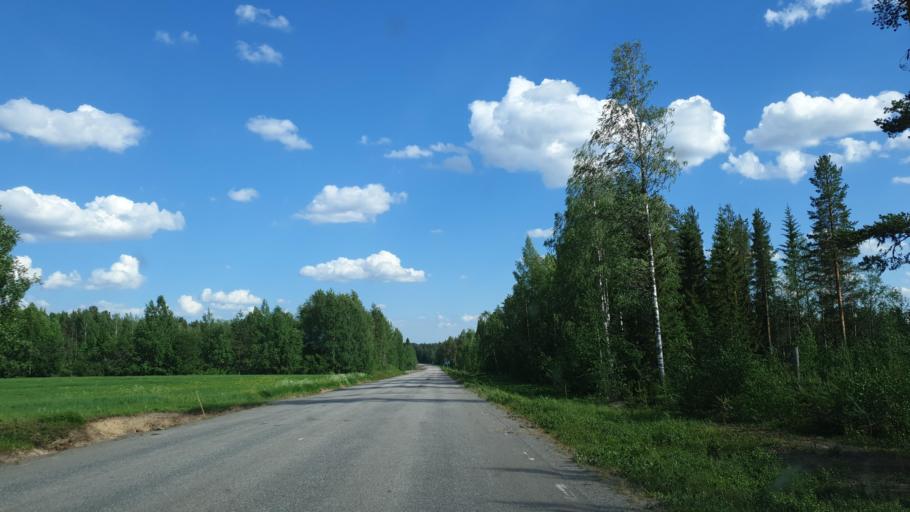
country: SE
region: Norrbotten
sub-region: Alvsbyns Kommun
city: AElvsbyn
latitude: 65.8390
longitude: 20.5102
